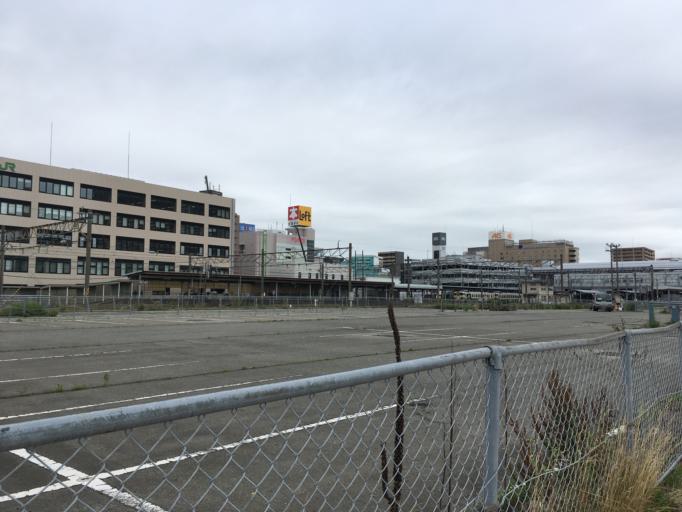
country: JP
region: Akita
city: Akita
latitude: 39.7143
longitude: 140.1305
